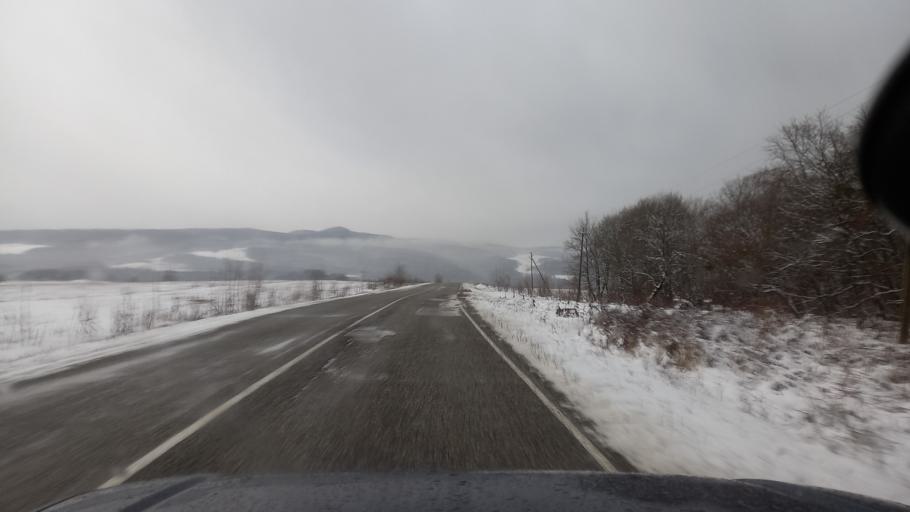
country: RU
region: Adygeya
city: Abadzekhskaya
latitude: 44.3444
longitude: 40.3585
